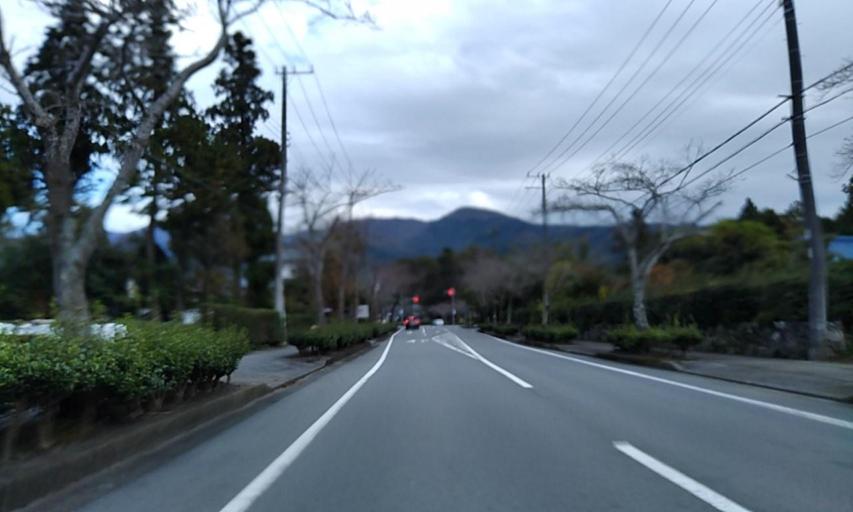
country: JP
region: Shizuoka
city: Gotemba
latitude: 35.2892
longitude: 138.9430
